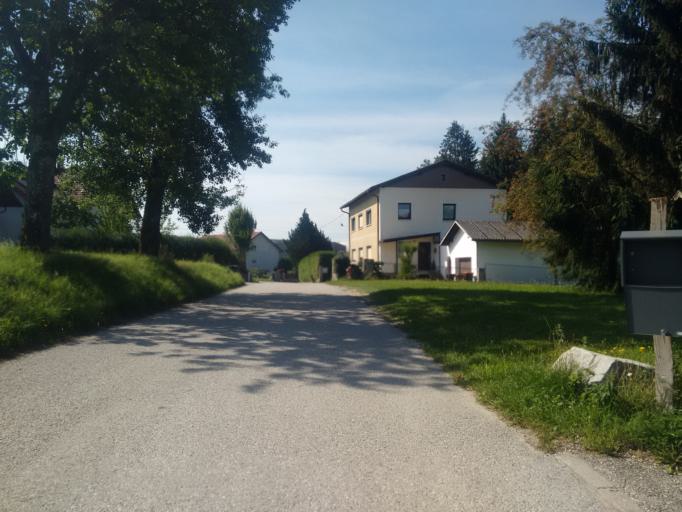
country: AT
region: Upper Austria
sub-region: Politischer Bezirk Grieskirchen
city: Bad Schallerbach
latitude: 48.1940
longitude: 13.9429
